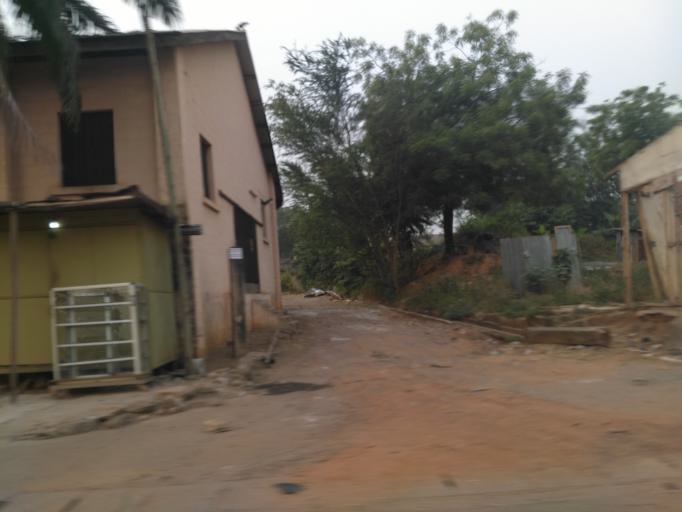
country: GH
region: Ashanti
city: Kumasi
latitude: 6.6868
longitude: -1.6180
